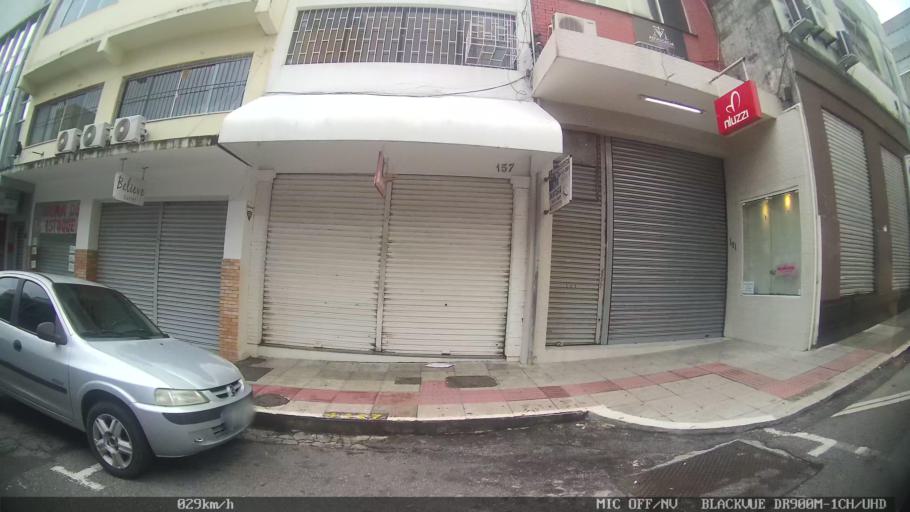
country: BR
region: Santa Catarina
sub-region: Florianopolis
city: Florianopolis
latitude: -27.5957
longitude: -48.5534
